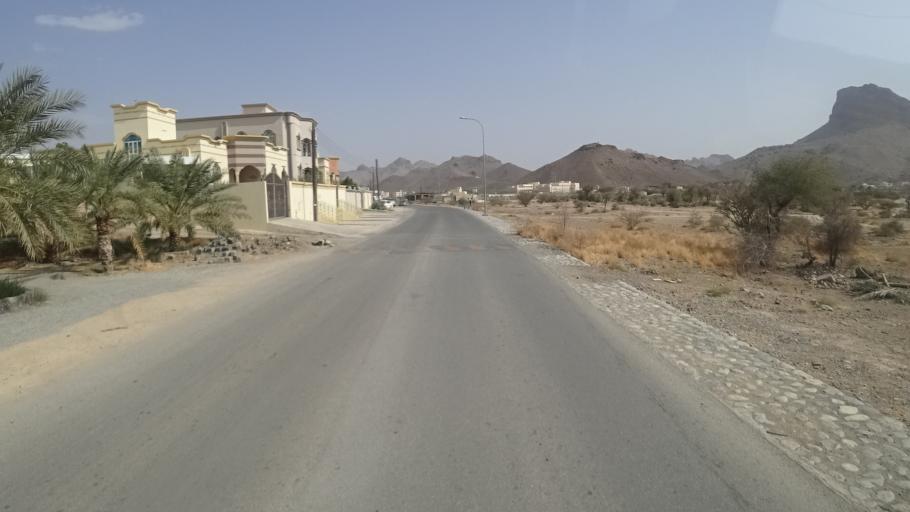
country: OM
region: Muhafazat ad Dakhiliyah
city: Bahla'
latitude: 23.0917
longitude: 57.3124
